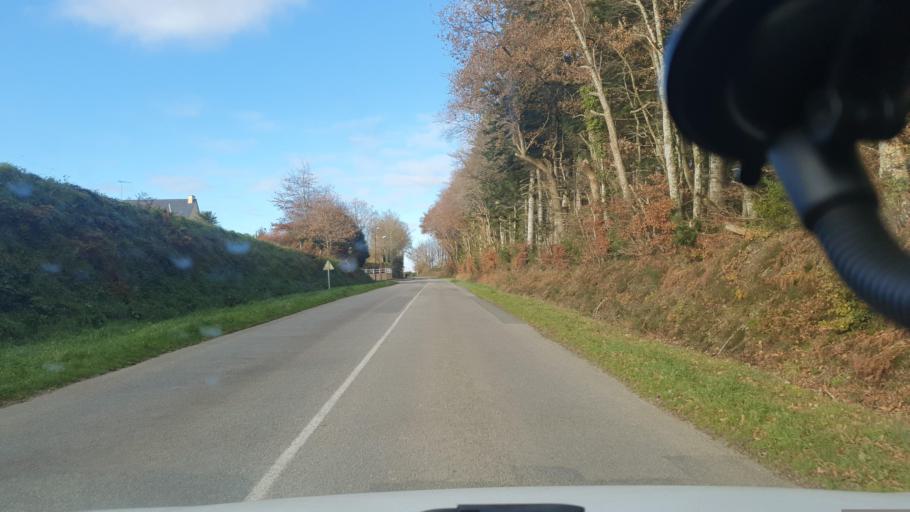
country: FR
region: Brittany
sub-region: Departement du Finistere
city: Briec
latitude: 48.0911
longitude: -3.9935
